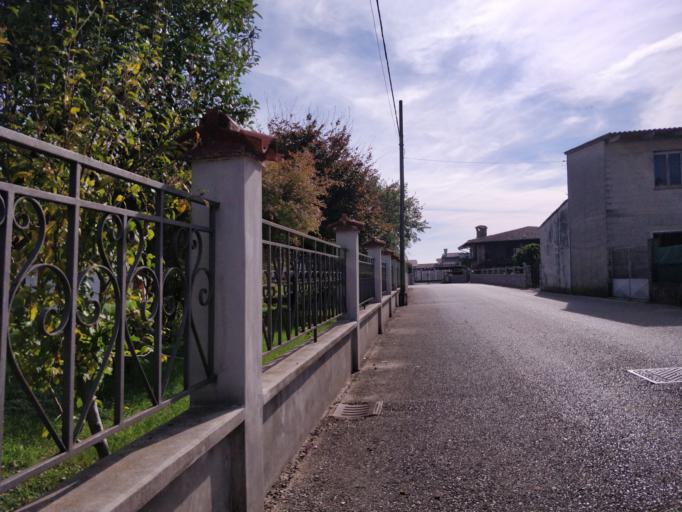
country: IT
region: Friuli Venezia Giulia
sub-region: Provincia di Udine
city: Bertiolo
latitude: 45.9414
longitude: 13.0458
